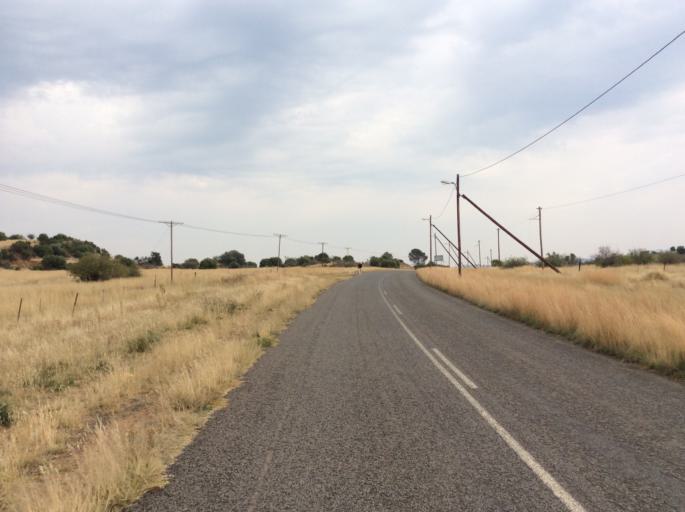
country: LS
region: Mafeteng
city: Mafeteng
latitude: -29.9875
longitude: 27.0259
